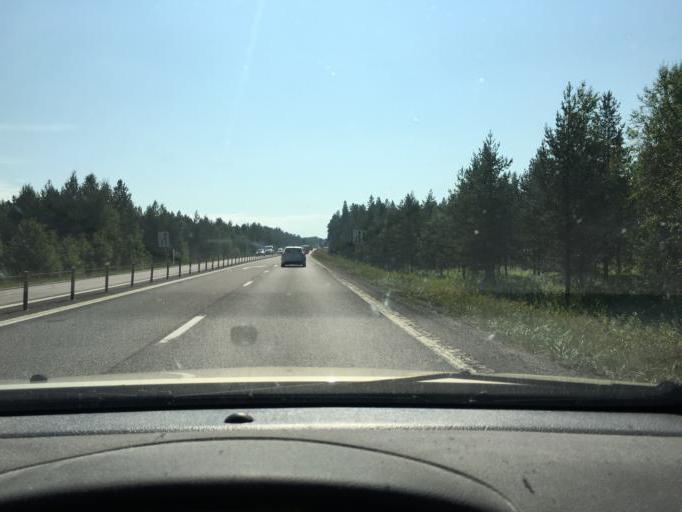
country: SE
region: Norrbotten
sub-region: Lulea Kommun
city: Gammelstad
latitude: 65.6096
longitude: 22.0517
